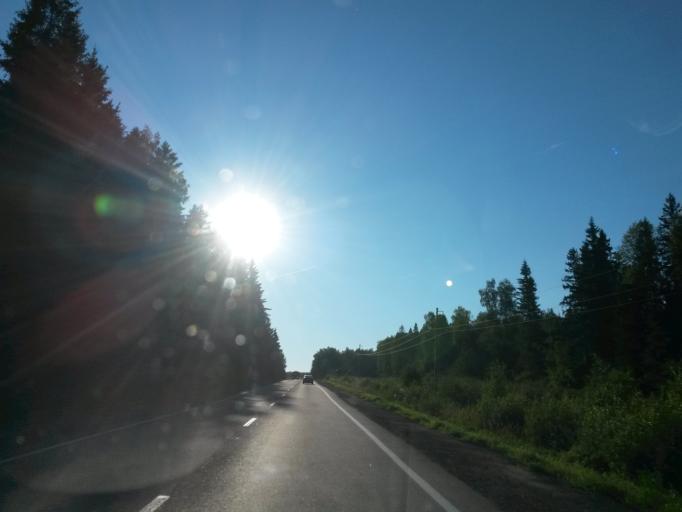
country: RU
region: Jaroslavl
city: Gavrilov-Yam
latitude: 57.2680
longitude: 39.9809
